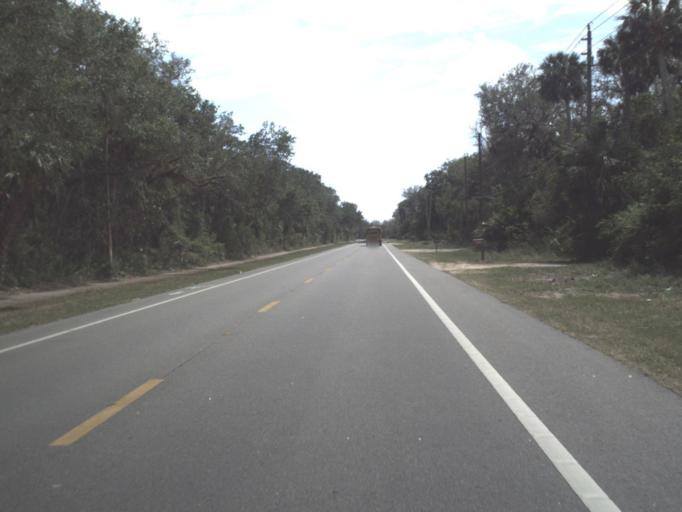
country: US
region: Florida
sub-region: Flagler County
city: Palm Coast
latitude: 29.5724
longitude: -81.1847
